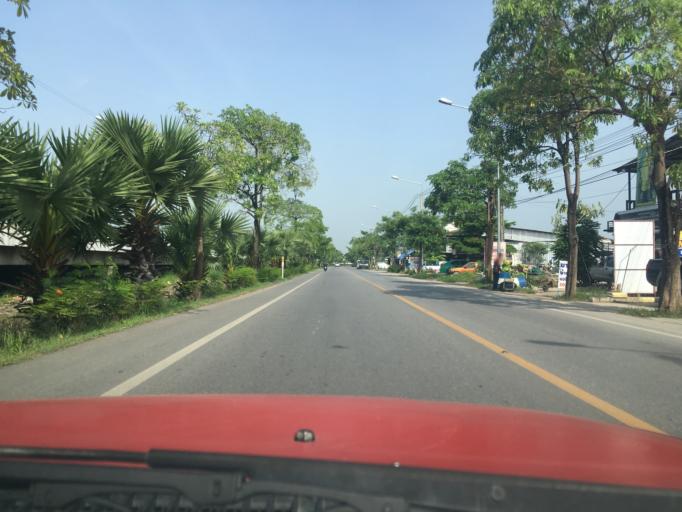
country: TH
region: Bangkok
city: Bang Khun Thian
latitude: 13.6273
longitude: 100.4277
